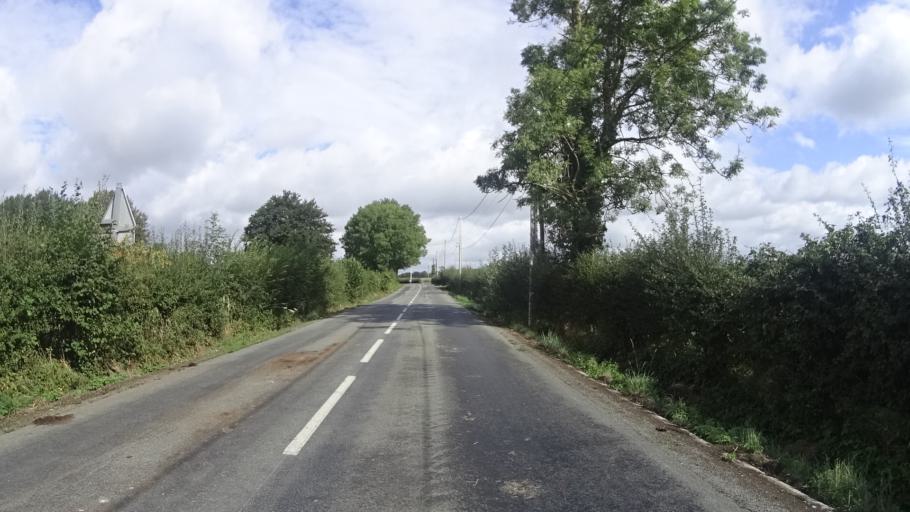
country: FR
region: Nord-Pas-de-Calais
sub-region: Departement du Nord
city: Landrecies
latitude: 50.0789
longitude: 3.6497
